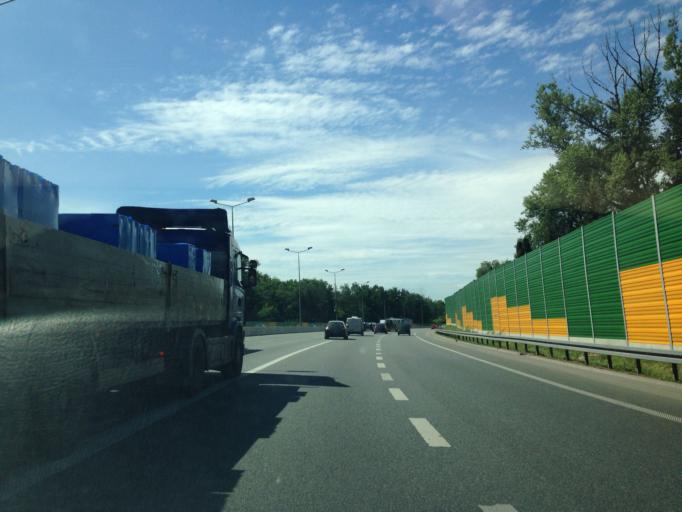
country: PL
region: Masovian Voivodeship
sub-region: Warszawa
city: Bemowo
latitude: 52.2533
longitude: 20.9443
